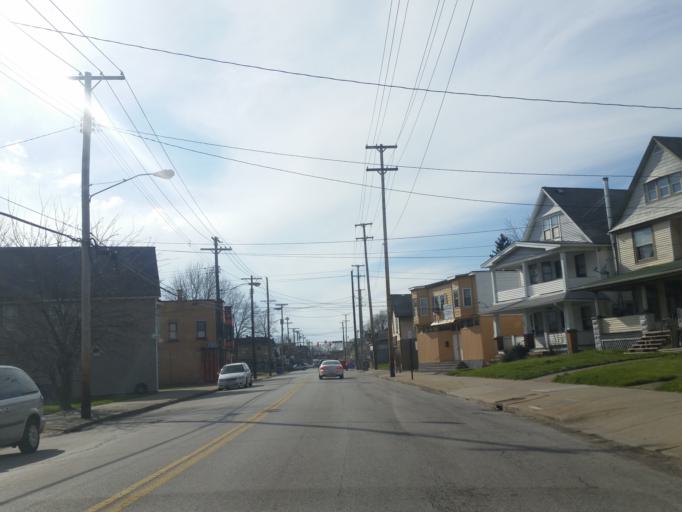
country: US
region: Ohio
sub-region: Cuyahoga County
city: Brooklyn
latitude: 41.4655
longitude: -81.7492
